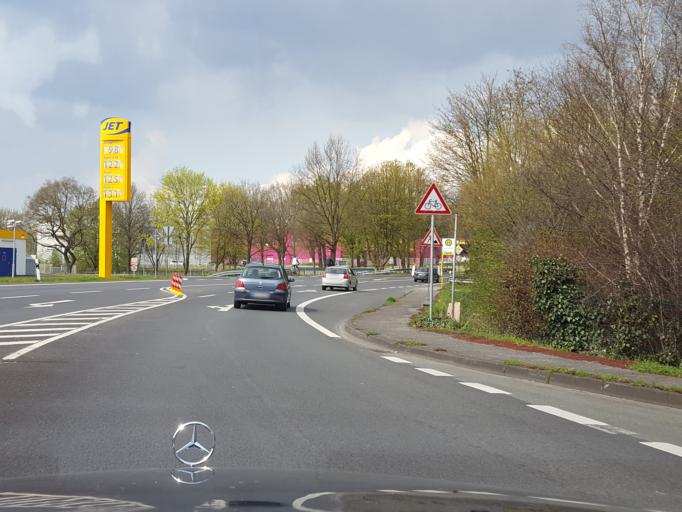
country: DE
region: North Rhine-Westphalia
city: Oer-Erkenschwick
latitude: 51.6365
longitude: 7.2824
